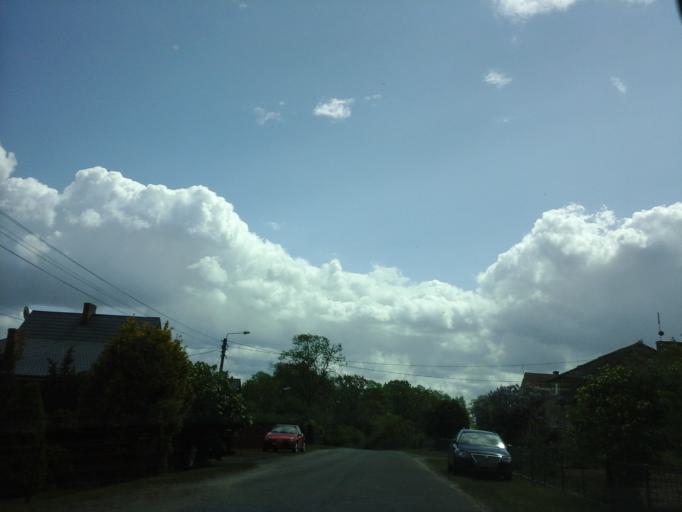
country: PL
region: West Pomeranian Voivodeship
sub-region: Powiat choszczenski
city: Choszczno
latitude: 53.1091
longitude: 15.4046
